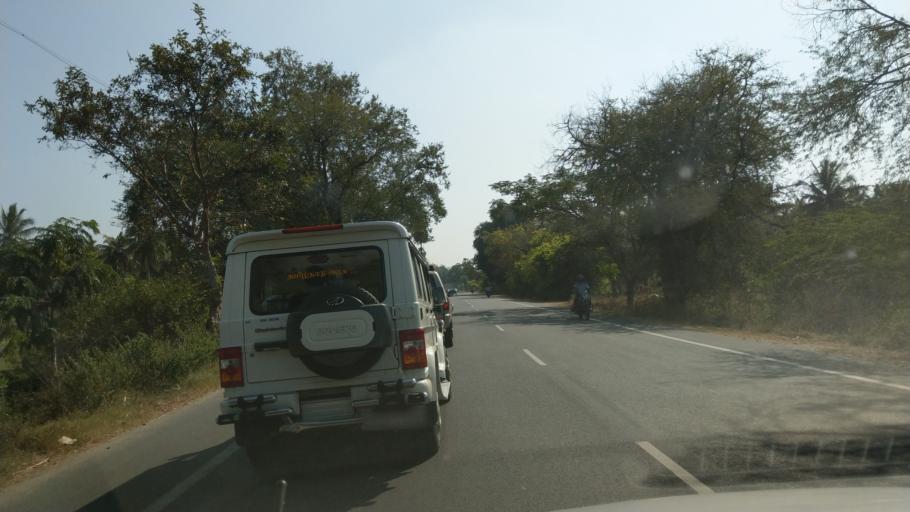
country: IN
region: Tamil Nadu
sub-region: Vellore
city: Arcot
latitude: 12.8821
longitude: 79.3171
